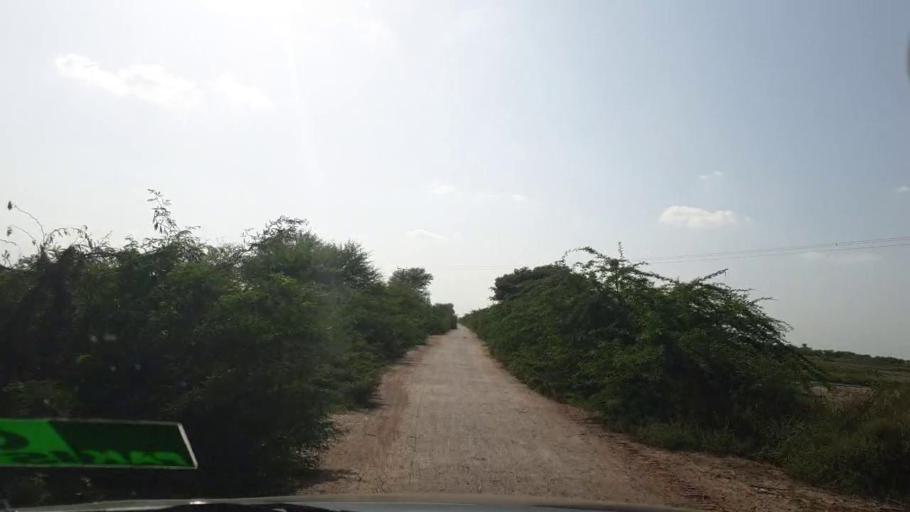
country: PK
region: Sindh
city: Naukot
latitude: 24.7117
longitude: 69.2064
